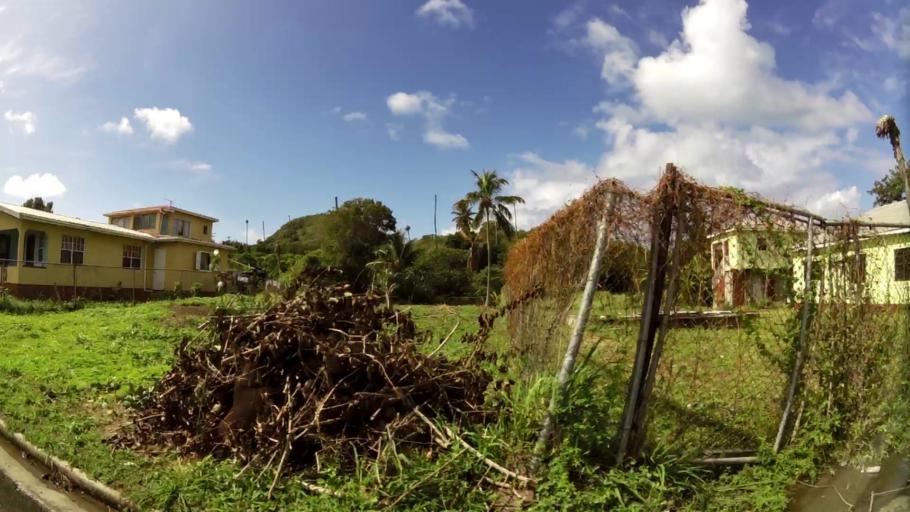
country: AG
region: Saint Mary
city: Bolands
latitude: 17.0669
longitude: -61.8759
